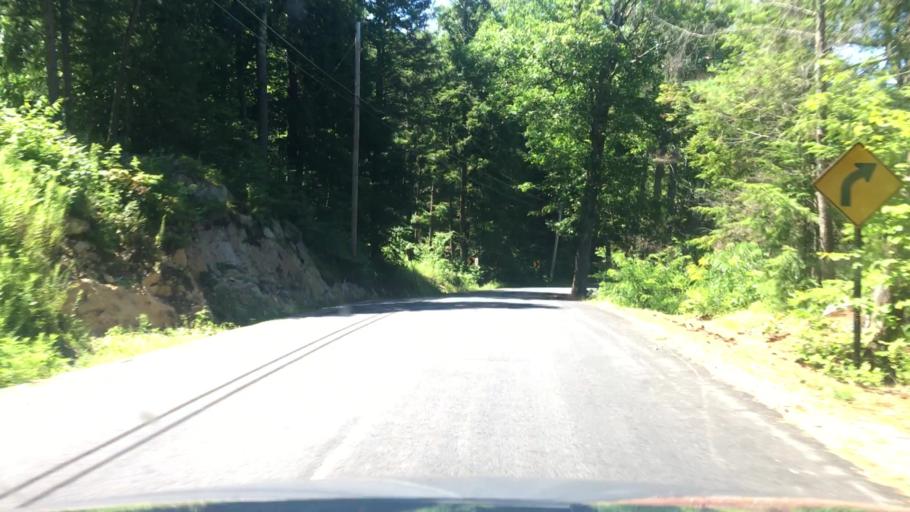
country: US
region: New Hampshire
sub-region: Merrimack County
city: Hopkinton
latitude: 43.2399
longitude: -71.6251
